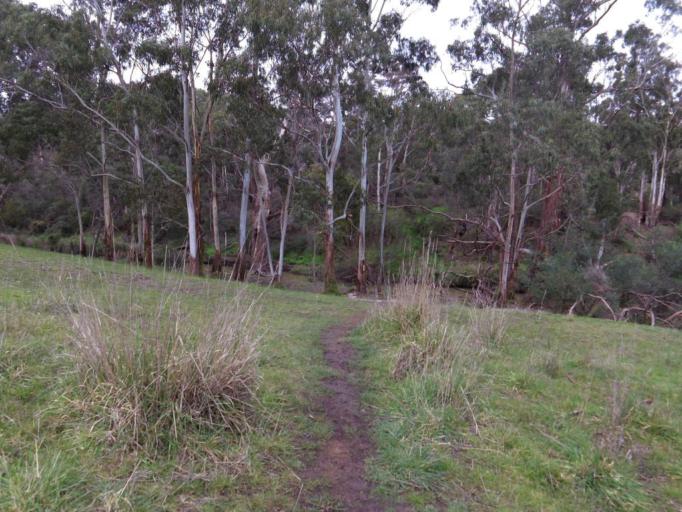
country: AU
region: Victoria
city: Plenty
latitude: -37.6382
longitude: 145.1030
